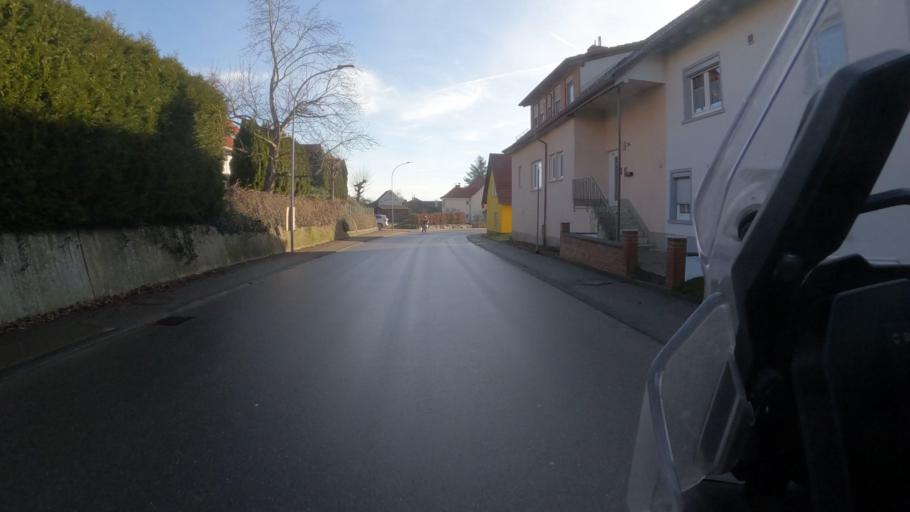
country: DE
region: Baden-Wuerttemberg
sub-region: Freiburg Region
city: Neuhausen
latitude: 47.8372
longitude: 8.7759
